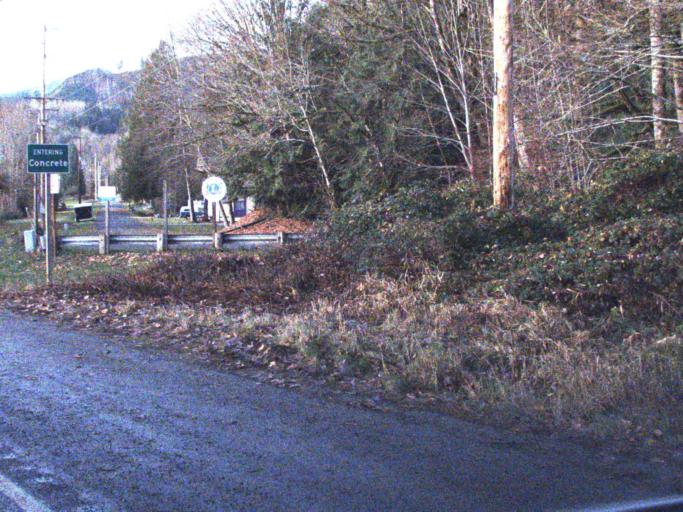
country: US
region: Washington
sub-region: Snohomish County
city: Darrington
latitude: 48.5349
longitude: -121.7334
